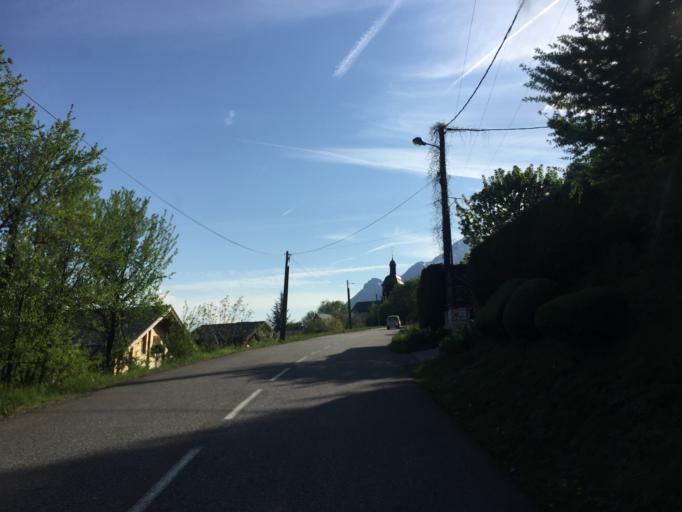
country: FR
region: Rhone-Alpes
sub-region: Departement de la Savoie
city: Mercury
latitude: 45.6667
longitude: 6.3186
